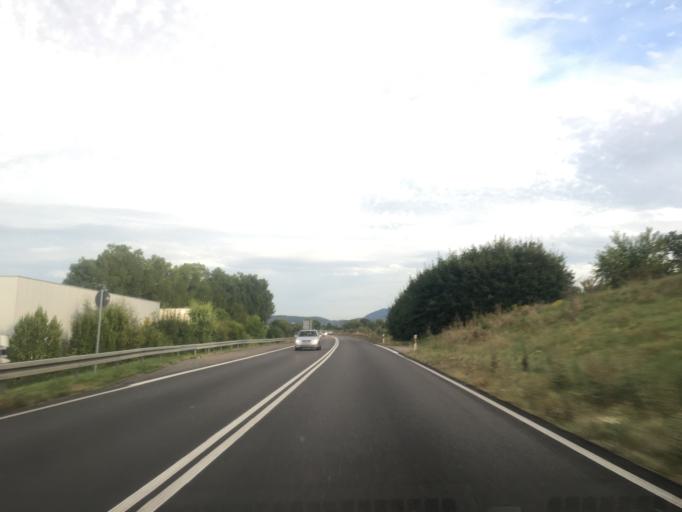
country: DE
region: Baden-Wuerttemberg
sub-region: Regierungsbezirk Stuttgart
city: Bempflingen
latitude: 48.5760
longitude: 9.2548
